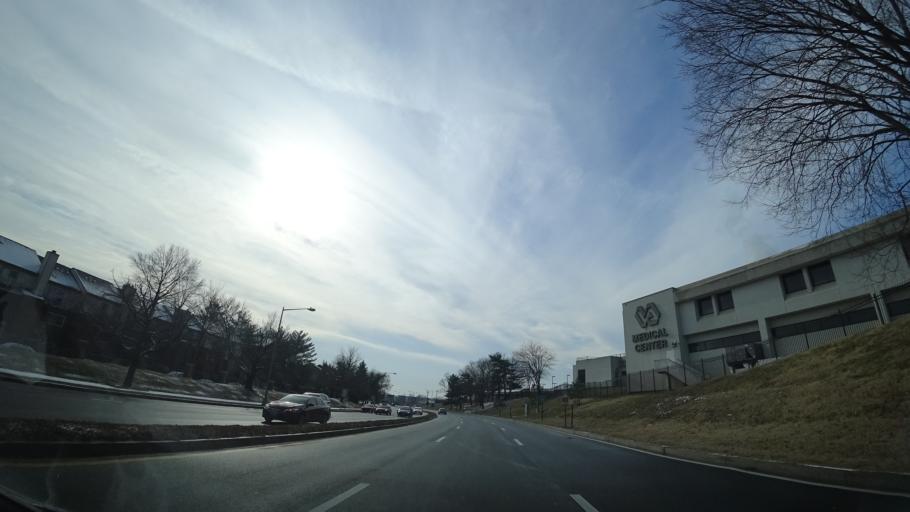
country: US
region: Maryland
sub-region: Prince George's County
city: Chillum
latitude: 38.9289
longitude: -77.0085
